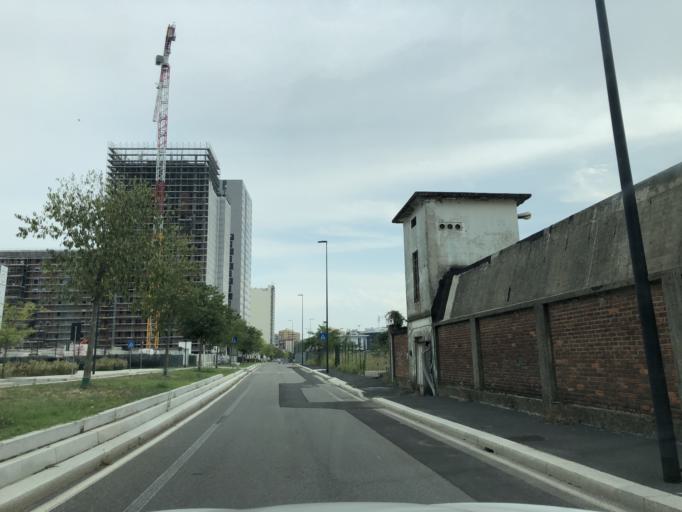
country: IT
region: Lombardy
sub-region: Citta metropolitana di Milano
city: Pero
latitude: 45.5105
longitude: 9.0991
